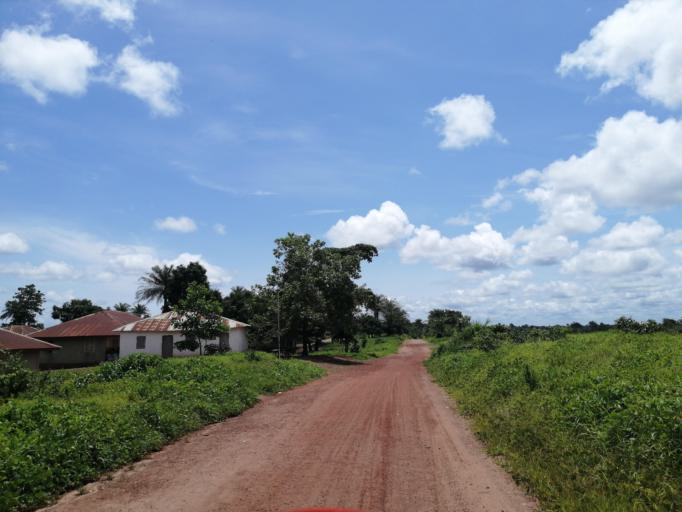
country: SL
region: Northern Province
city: Pepel
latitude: 8.6564
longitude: -13.0060
